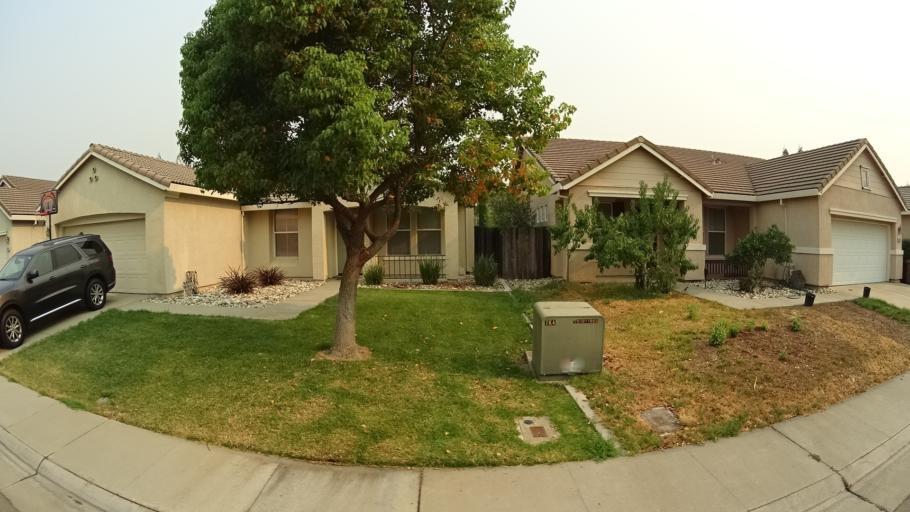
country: US
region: California
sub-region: Sacramento County
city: Laguna
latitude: 38.4042
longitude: -121.4454
